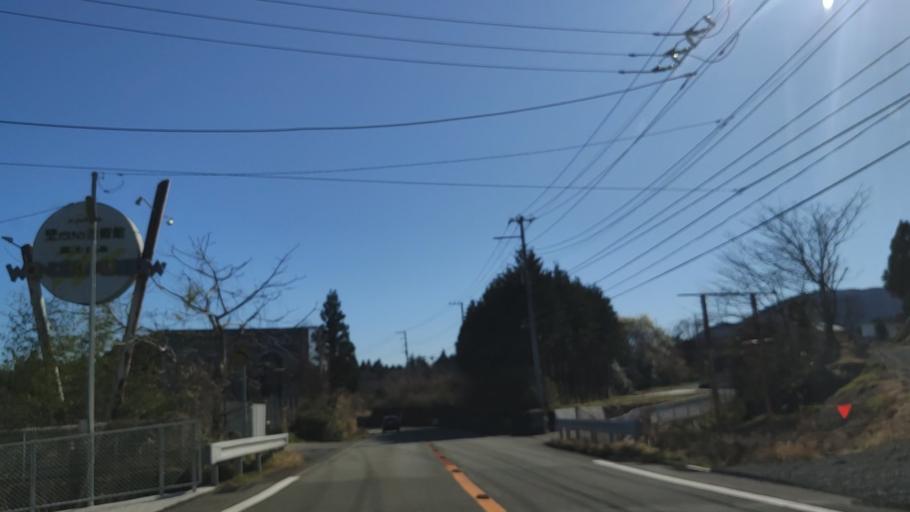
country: JP
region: Shizuoka
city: Fujinomiya
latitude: 35.3194
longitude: 138.5853
